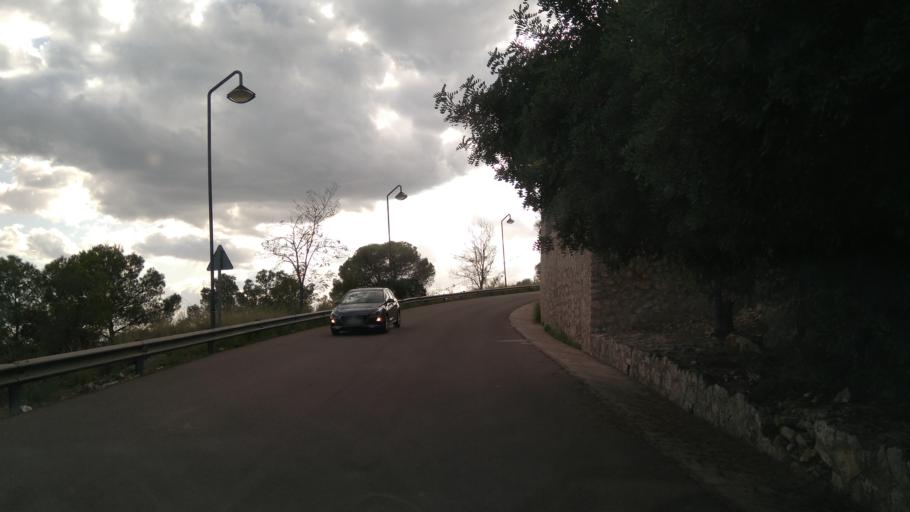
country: ES
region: Valencia
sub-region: Provincia de Valencia
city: Alzira
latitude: 39.1528
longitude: -0.4174
